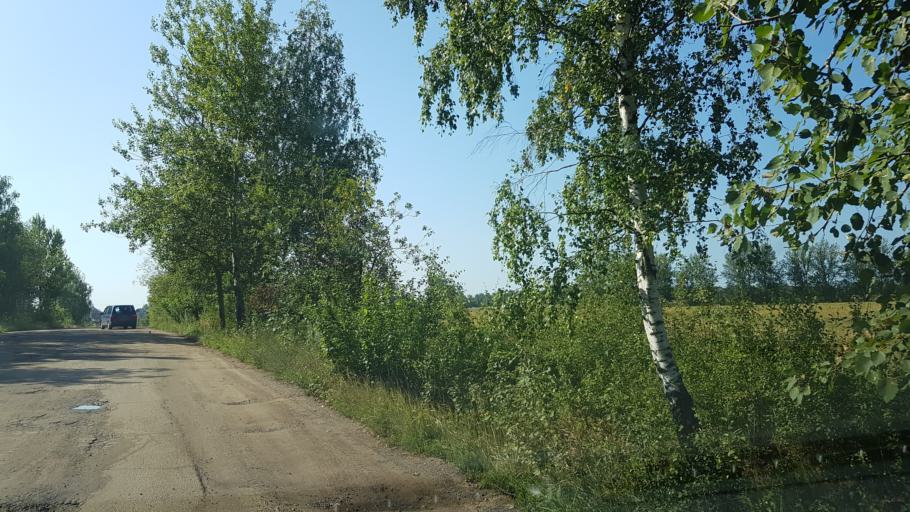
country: BY
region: Mogilev
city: Babruysk
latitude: 53.1174
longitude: 29.1887
